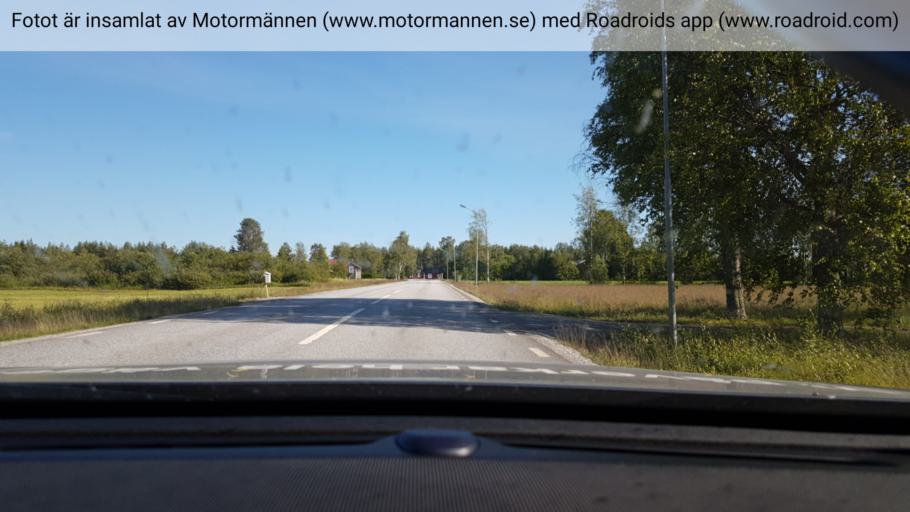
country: SE
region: Vaesterbotten
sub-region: Vindelns Kommun
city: Vindeln
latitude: 64.1224
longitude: 19.5606
